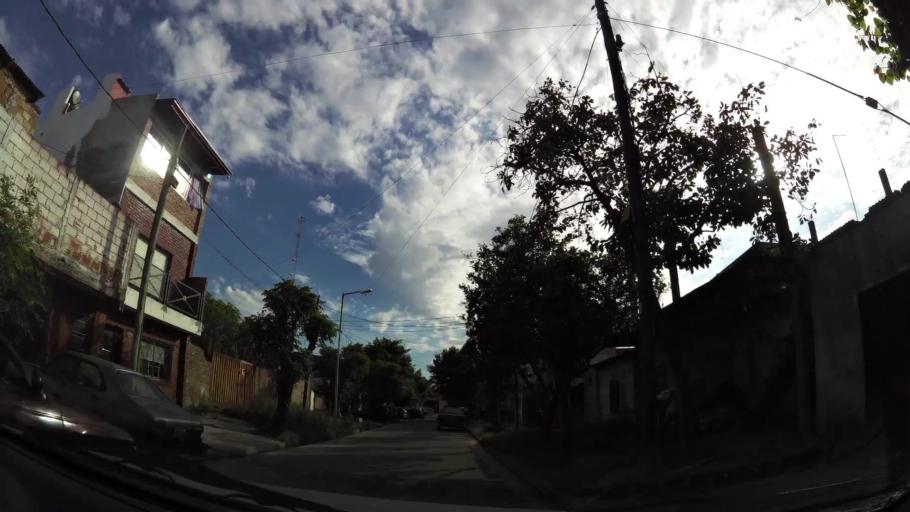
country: AR
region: Buenos Aires
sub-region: Partido de Lanus
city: Lanus
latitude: -34.7039
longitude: -58.3538
